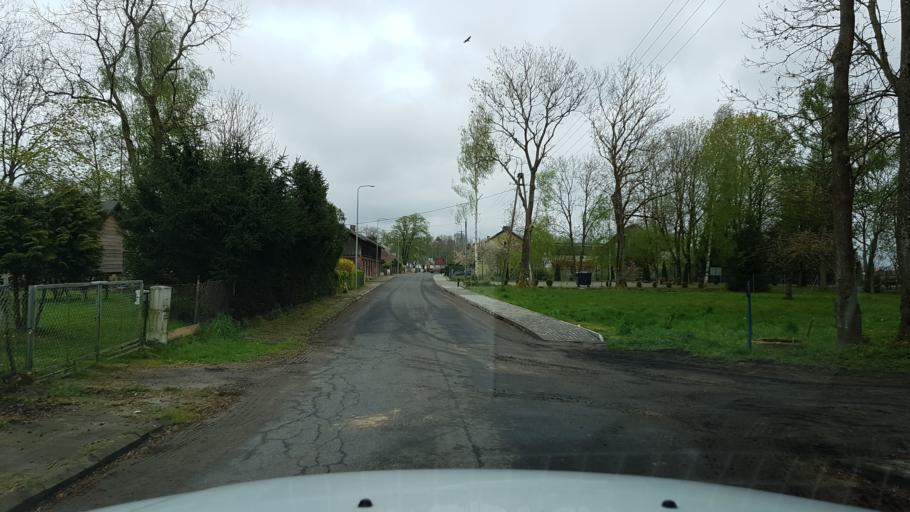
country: PL
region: West Pomeranian Voivodeship
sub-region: Powiat kolobrzeski
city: Ryman
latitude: 54.0304
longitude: 15.5266
